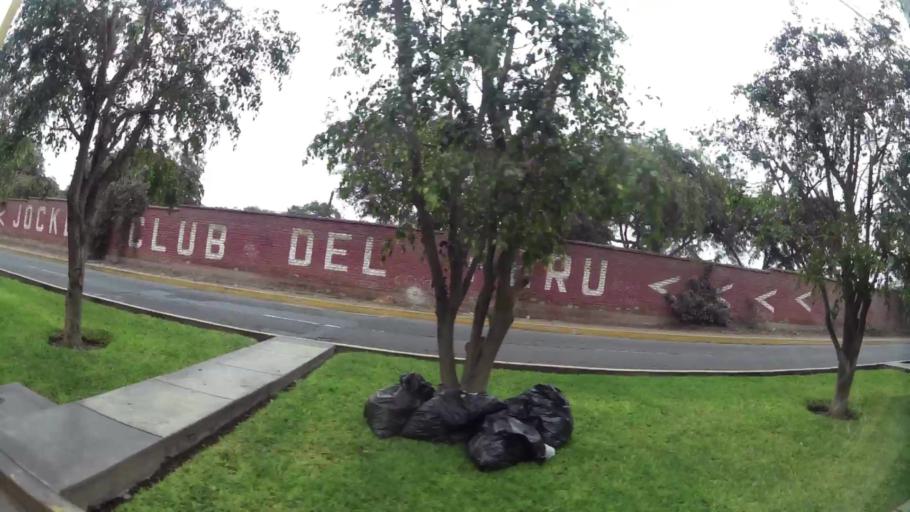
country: PE
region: Lima
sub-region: Lima
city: La Molina
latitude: -12.0914
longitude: -76.9738
